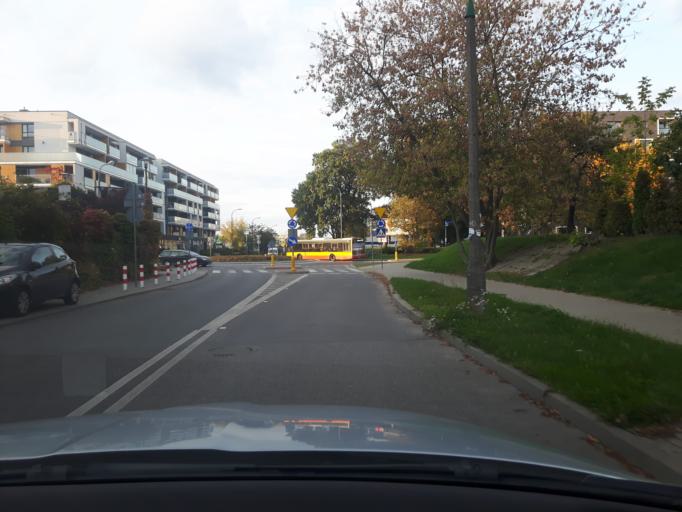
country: PL
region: Masovian Voivodeship
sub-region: Warszawa
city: Ursynow
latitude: 52.1552
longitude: 21.0216
